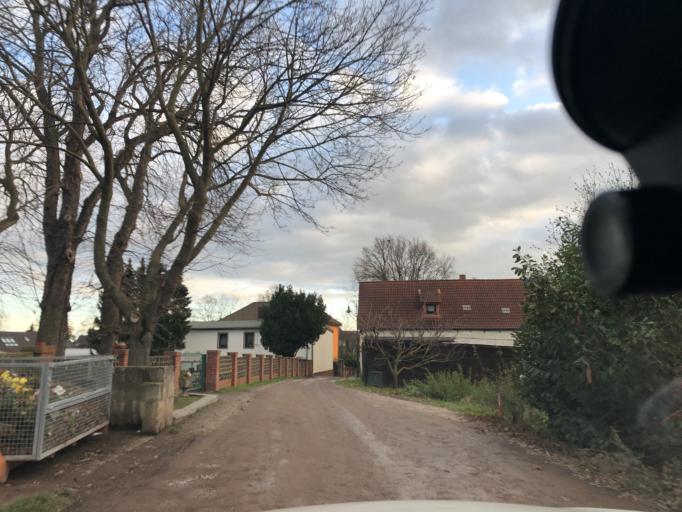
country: DE
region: Saxony-Anhalt
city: Zscherben
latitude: 51.4696
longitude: 11.8713
